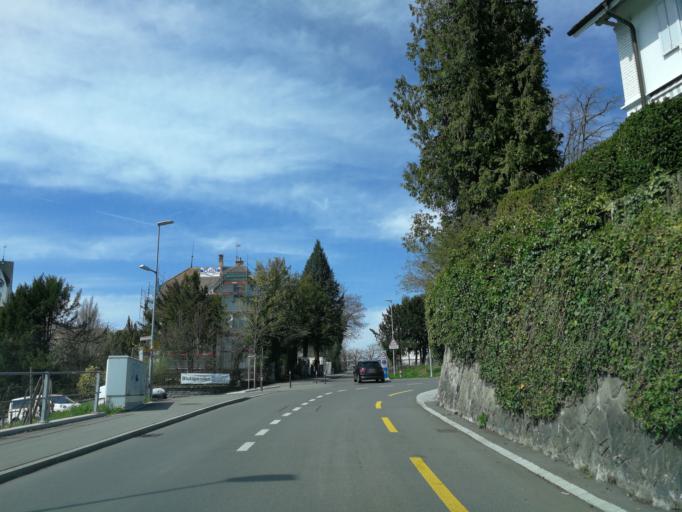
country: CH
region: Zurich
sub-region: Bezirk Meilen
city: Uetikon
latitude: 47.2617
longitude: 8.6795
